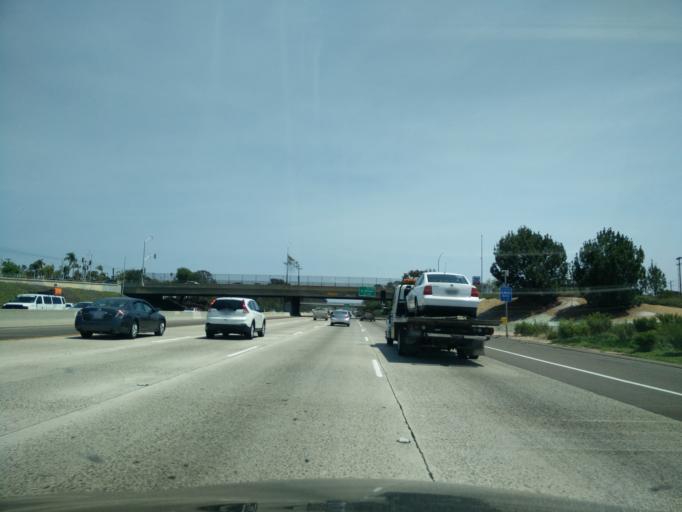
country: US
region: California
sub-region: San Diego County
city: Chula Vista
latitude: 32.6407
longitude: -117.1006
